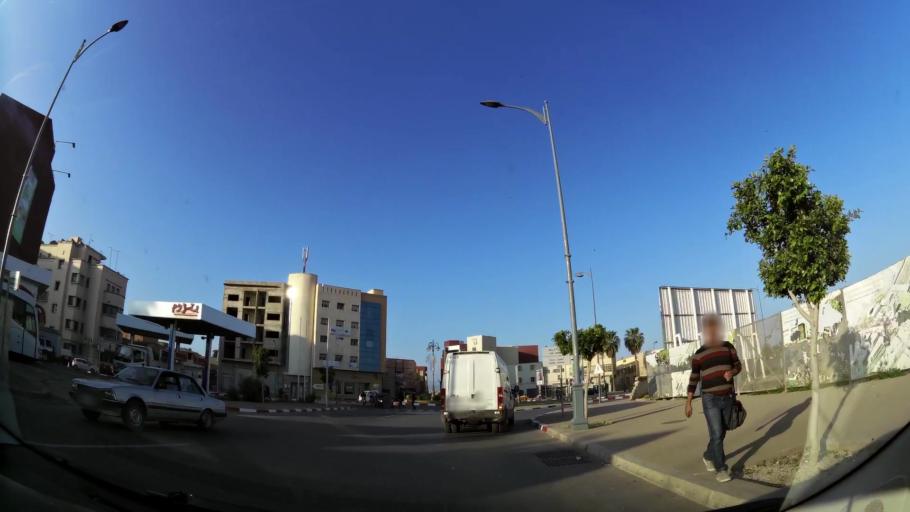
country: MA
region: Oriental
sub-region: Oujda-Angad
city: Oujda
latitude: 34.6762
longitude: -1.9251
